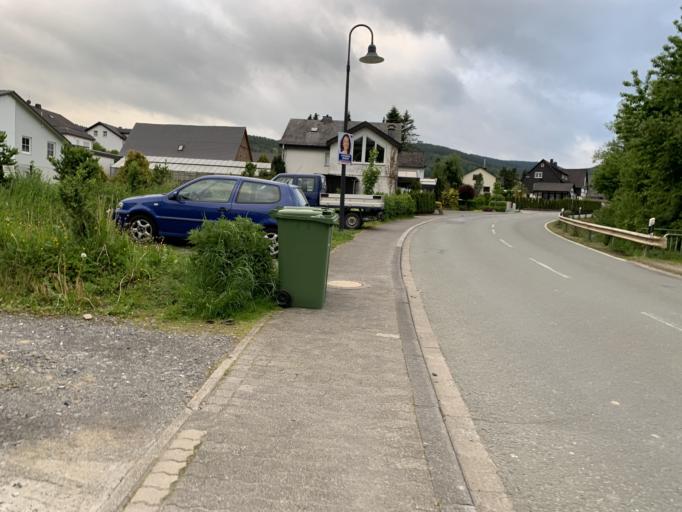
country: DE
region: North Rhine-Westphalia
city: Eslohe
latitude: 51.2873
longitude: 8.1736
